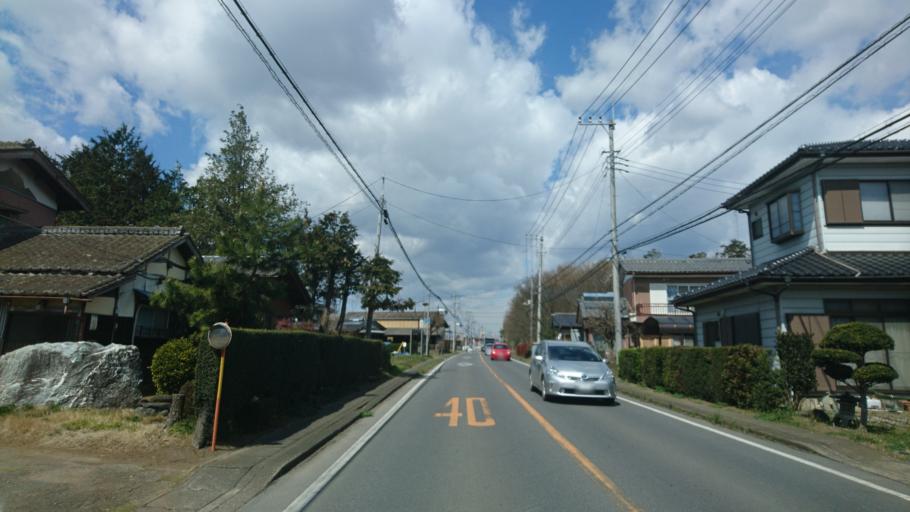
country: JP
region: Ibaraki
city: Ishige
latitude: 36.2036
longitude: 139.9447
